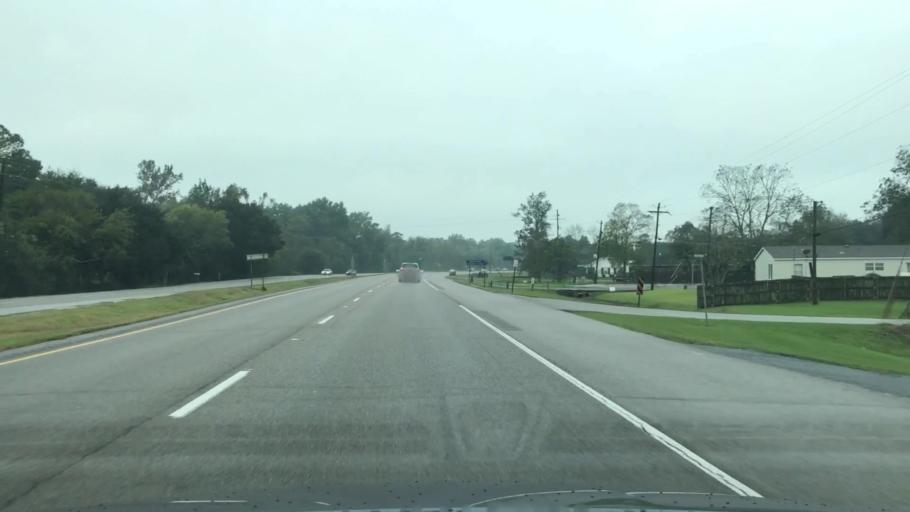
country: US
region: Louisiana
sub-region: Saint Charles Parish
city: Des Allemands
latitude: 29.8330
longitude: -90.4548
